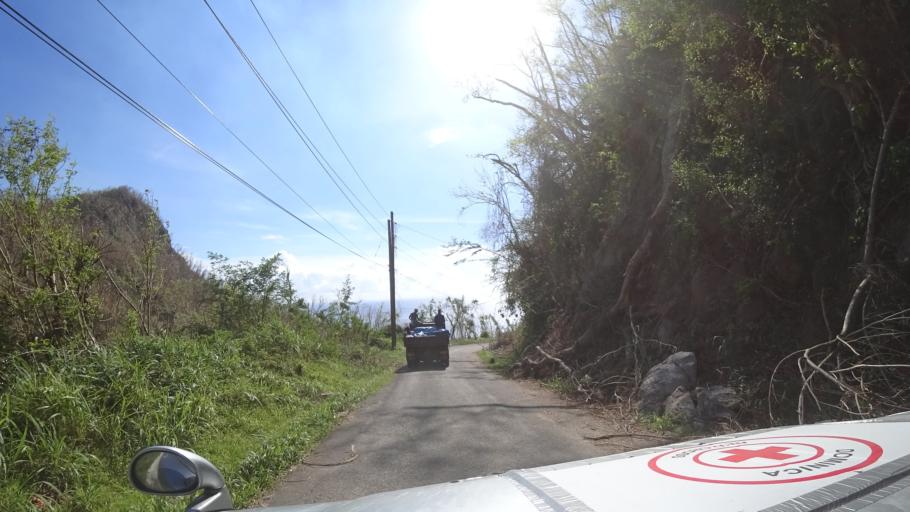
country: DM
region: Saint Mark
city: Soufriere
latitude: 15.2424
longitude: -61.3653
